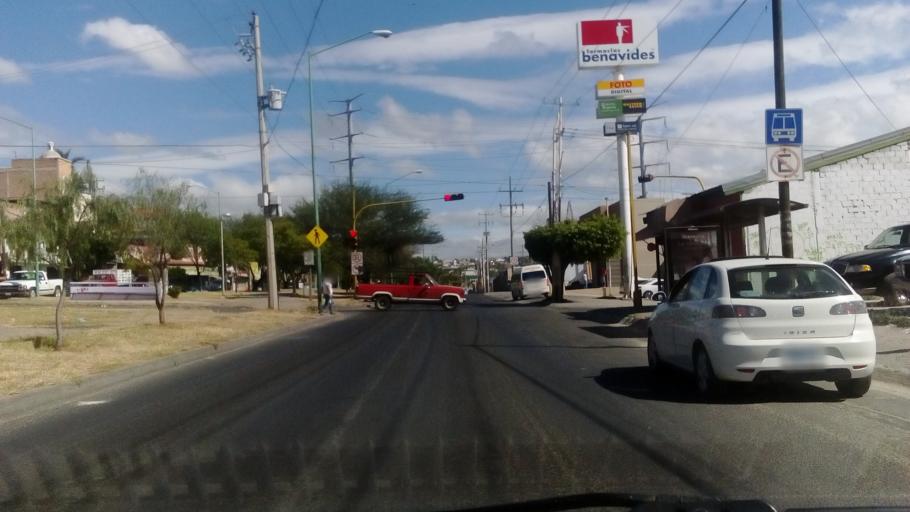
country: MX
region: Guanajuato
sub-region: Leon
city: Ejido la Joya
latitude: 21.1144
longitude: -101.7097
